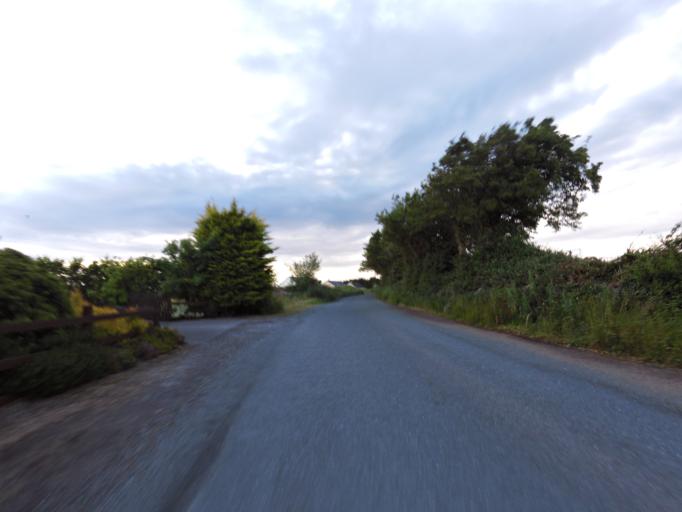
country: IE
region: Connaught
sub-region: County Galway
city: Athenry
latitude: 53.2949
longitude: -8.7314
